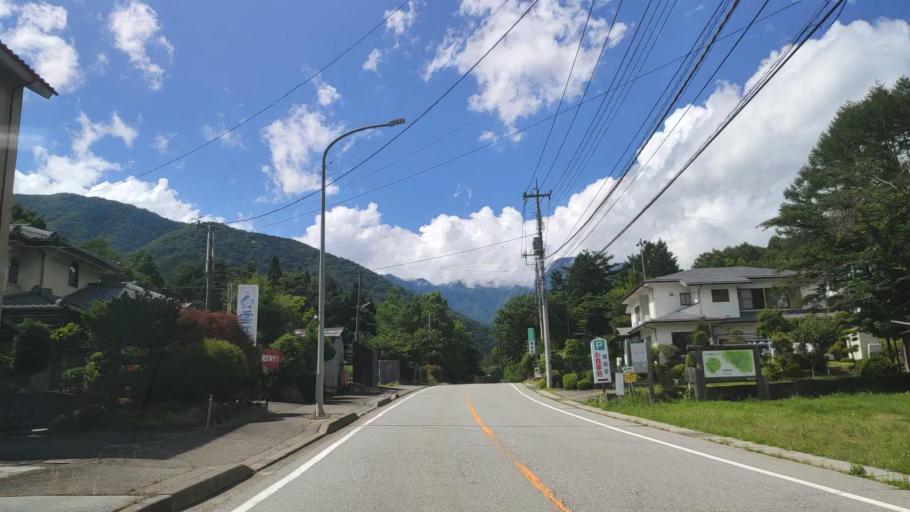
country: JP
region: Yamanashi
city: Enzan
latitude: 35.8484
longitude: 138.7606
